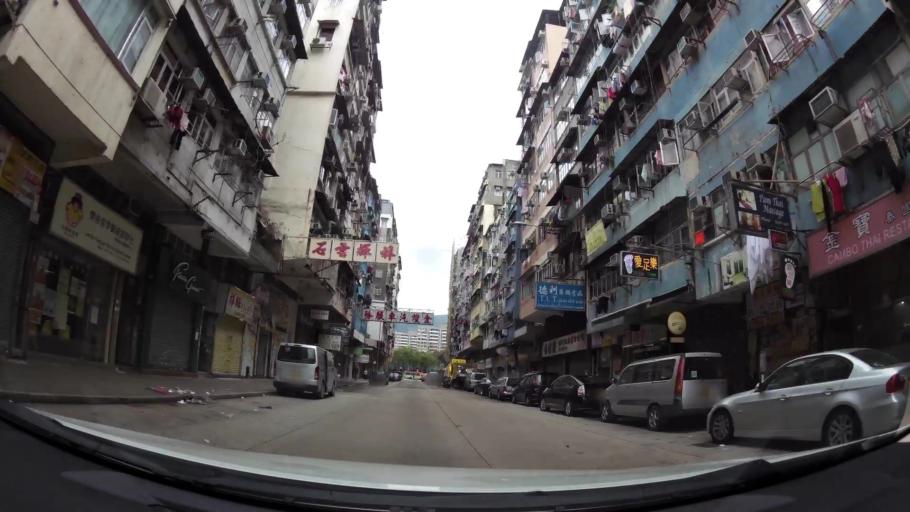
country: HK
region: Kowloon City
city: Kowloon
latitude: 22.3294
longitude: 114.1915
